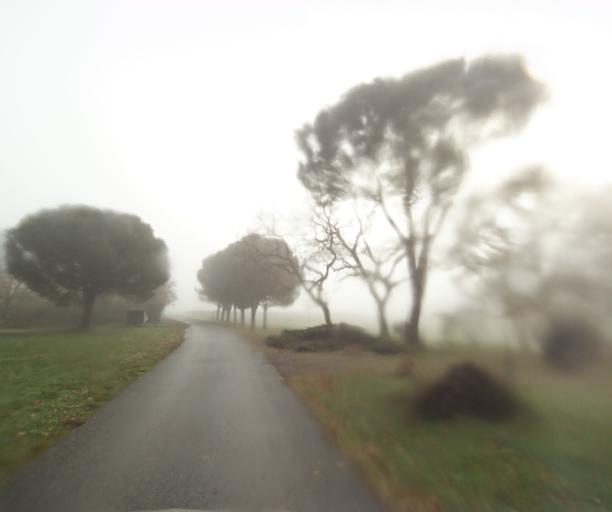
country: FR
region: Midi-Pyrenees
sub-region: Departement de la Haute-Garonne
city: Villaudric
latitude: 43.8197
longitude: 1.4617
